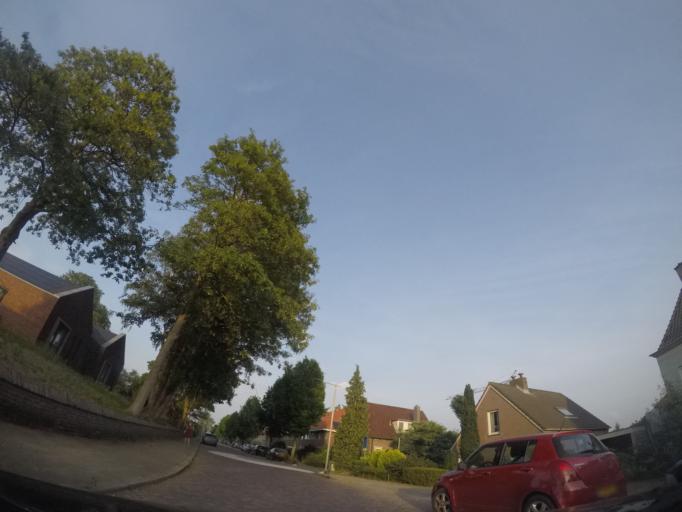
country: NL
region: Gelderland
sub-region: Gemeente Arnhem
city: Hoogkamp
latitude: 51.9827
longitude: 5.8700
